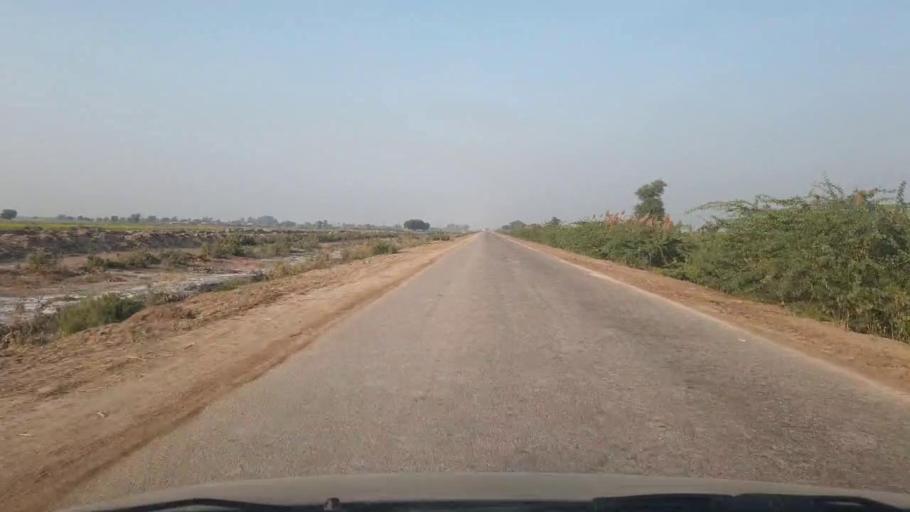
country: PK
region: Sindh
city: Mirwah Gorchani
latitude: 25.3334
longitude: 69.1673
